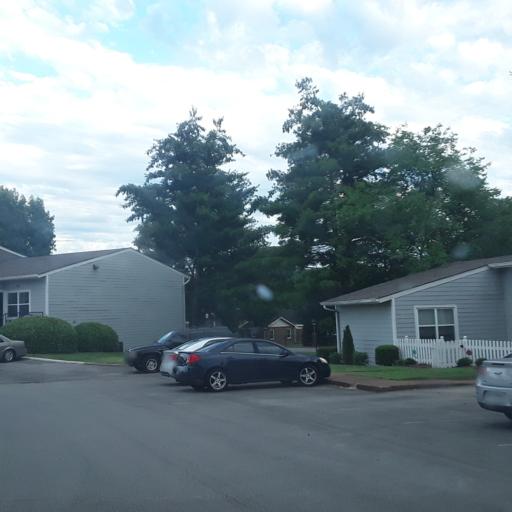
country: US
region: Tennessee
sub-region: Wilson County
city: Green Hill
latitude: 36.1620
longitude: -86.5966
